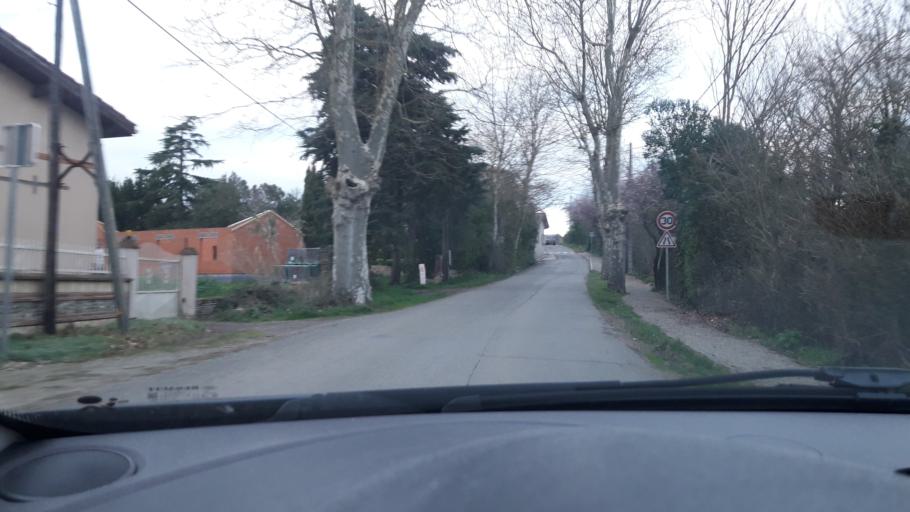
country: FR
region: Midi-Pyrenees
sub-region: Departement de la Haute-Garonne
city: Launac
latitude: 43.7127
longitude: 1.0846
